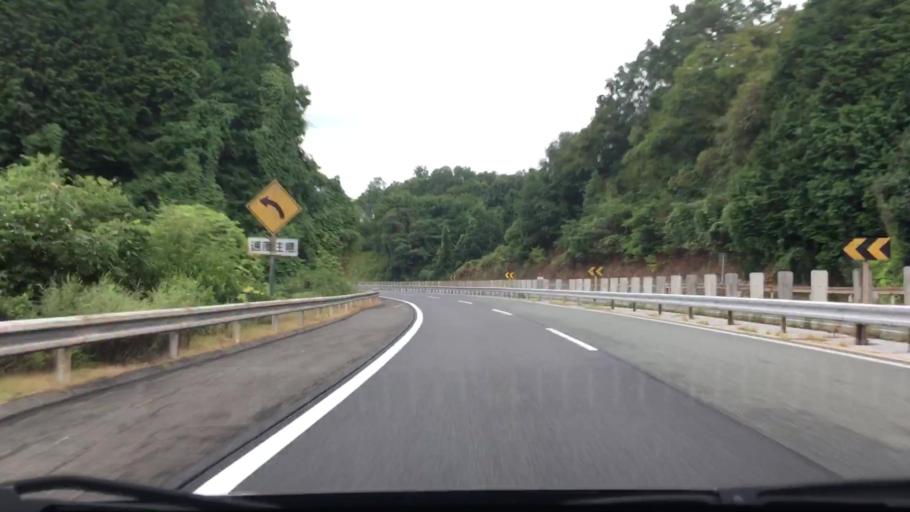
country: JP
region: Okayama
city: Niimi
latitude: 34.9100
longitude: 133.3030
